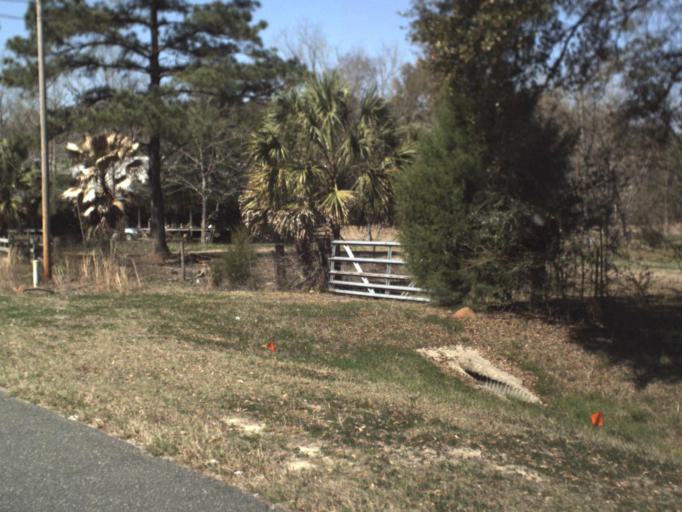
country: US
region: Florida
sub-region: Washington County
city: Chipley
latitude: 30.7873
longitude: -85.4381
